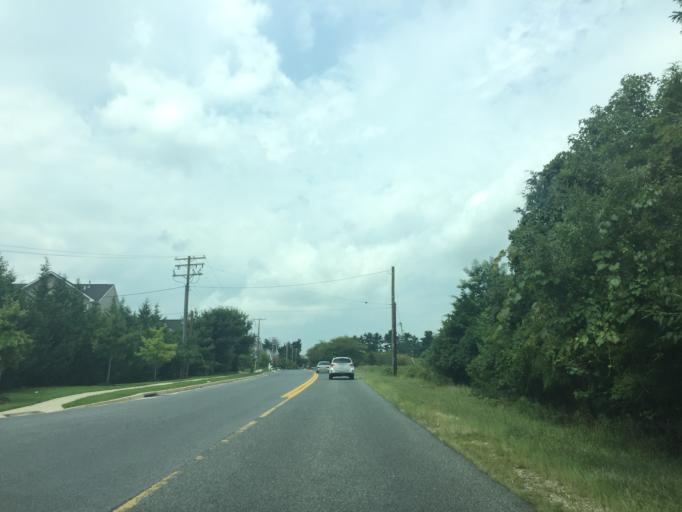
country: US
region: Maryland
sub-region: Baltimore County
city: White Marsh
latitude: 39.3975
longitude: -76.4327
